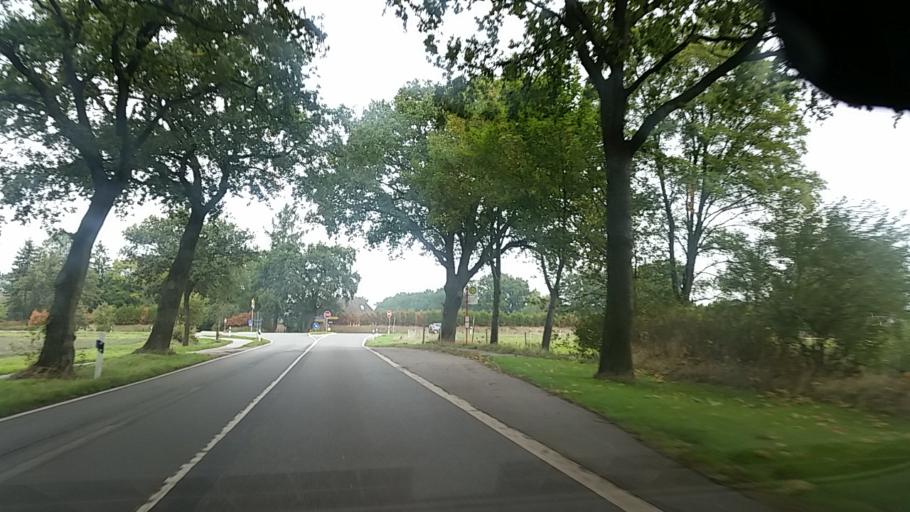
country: DE
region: Schleswig-Holstein
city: Hasenmoor
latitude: 53.8988
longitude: 9.9790
